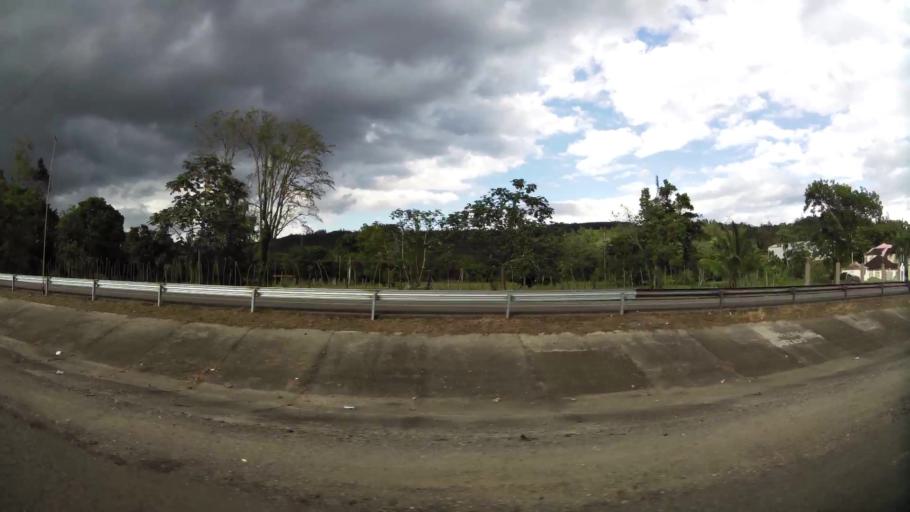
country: DO
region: Monsenor Nouel
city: Bonao
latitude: 18.9710
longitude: -70.4189
